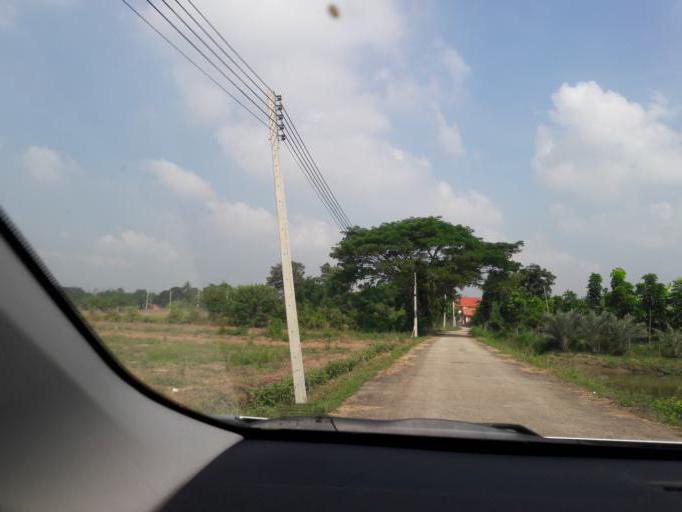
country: TH
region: Ang Thong
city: Ang Thong
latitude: 14.5467
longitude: 100.4395
